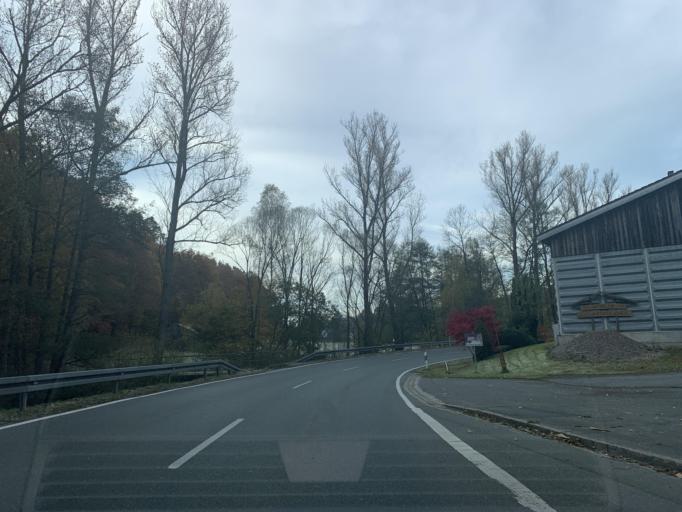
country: DE
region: Bavaria
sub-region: Upper Palatinate
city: Bach
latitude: 49.3812
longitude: 12.3807
